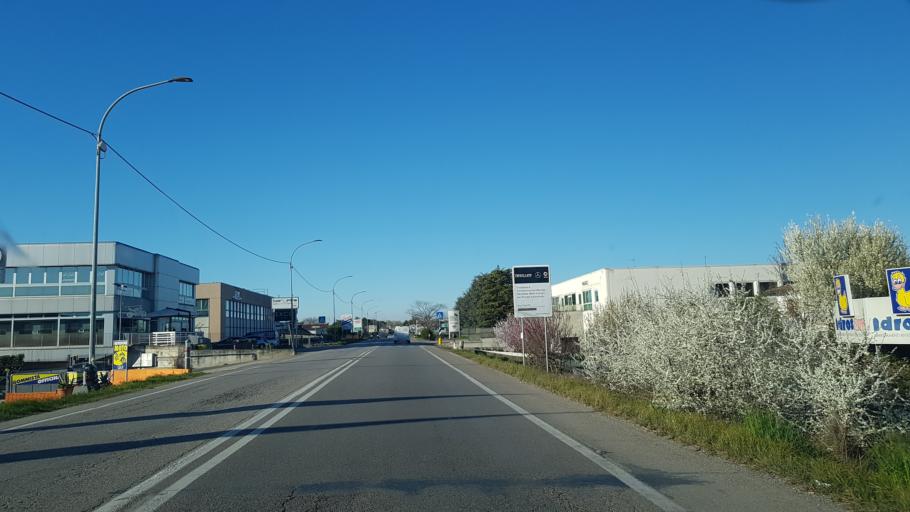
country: IT
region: Veneto
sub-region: Provincia di Padova
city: Boara Pisani
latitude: 45.0959
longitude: 11.7856
